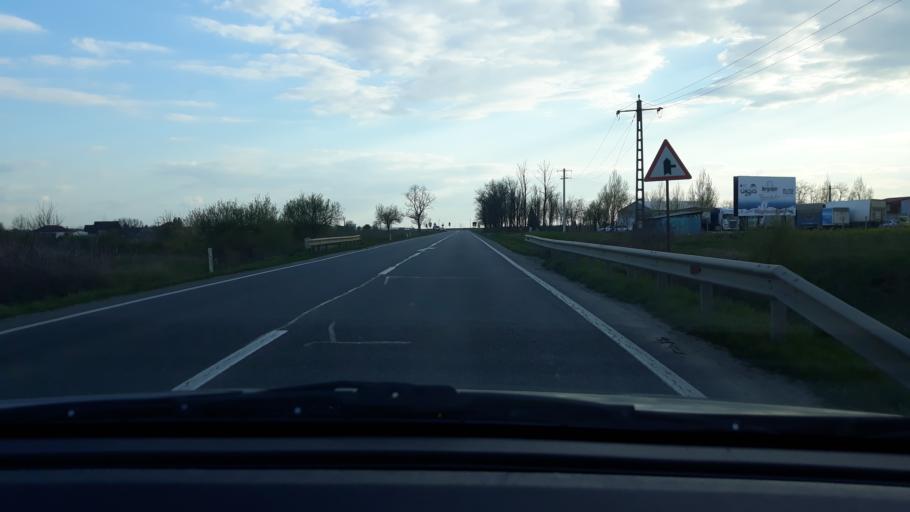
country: RO
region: Bihor
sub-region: Comuna Tamaseu
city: Tamaseu
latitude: 47.2065
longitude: 21.9222
